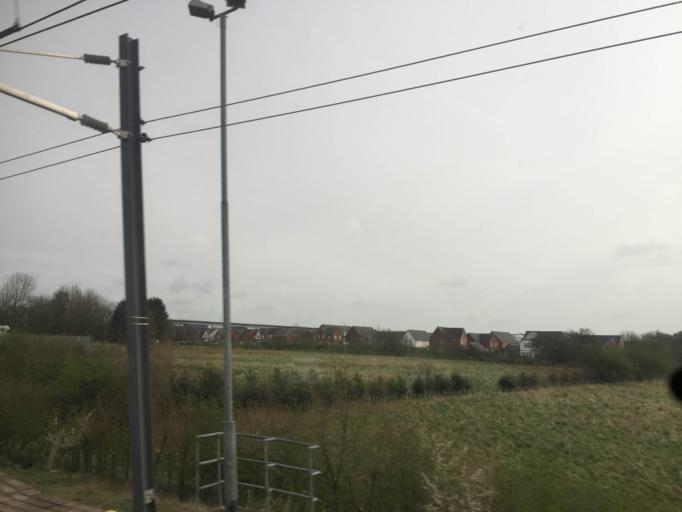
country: GB
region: England
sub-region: Lancashire
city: Euxton
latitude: 53.6797
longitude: -2.6781
